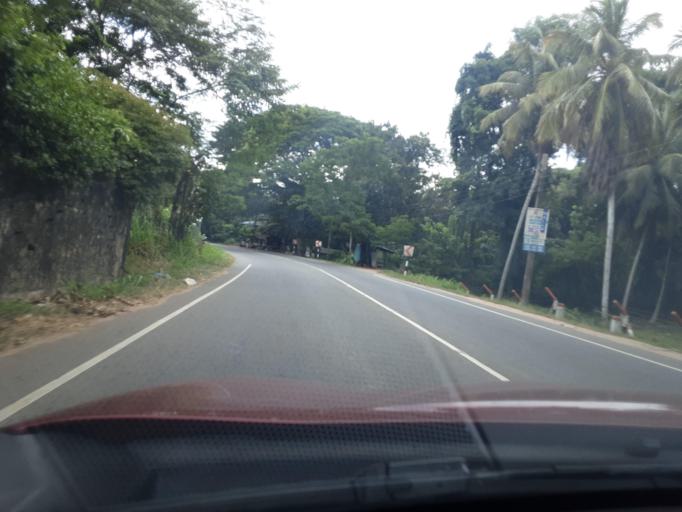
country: LK
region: North Western
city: Kurunegala
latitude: 7.4381
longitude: 80.2072
